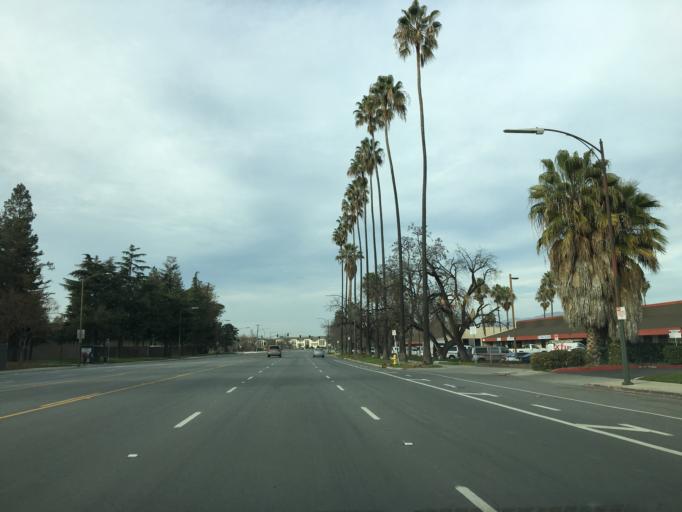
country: US
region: California
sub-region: Santa Clara County
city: San Jose
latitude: 37.3744
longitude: -121.8946
